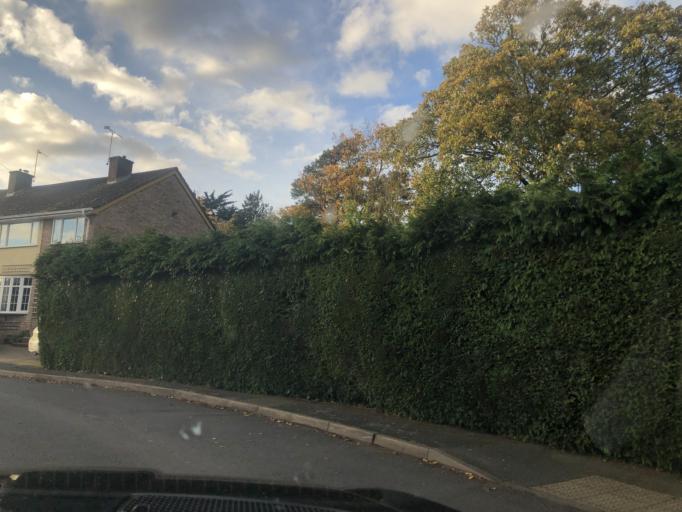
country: GB
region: England
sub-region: Warwickshire
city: Harbury
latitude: 52.2366
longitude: -1.4626
